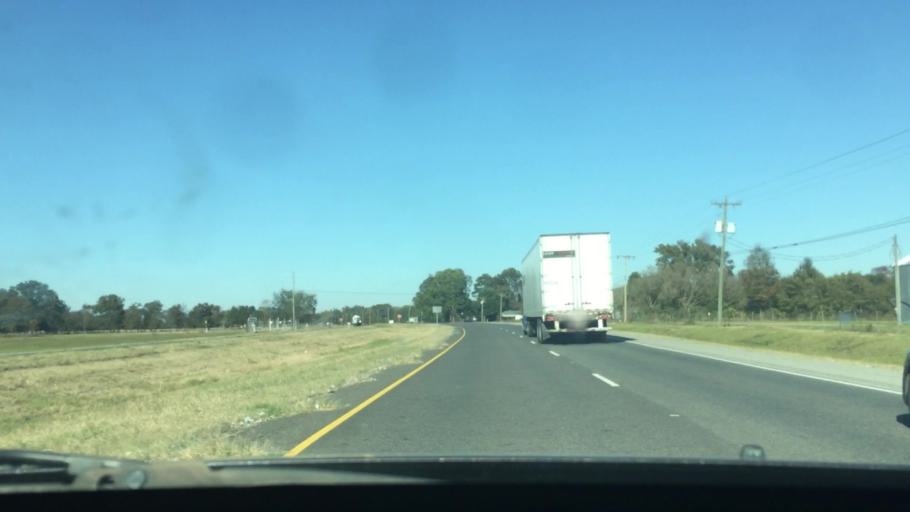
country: US
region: Louisiana
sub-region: Richland Parish
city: Rayville
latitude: 32.3762
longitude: -91.7700
